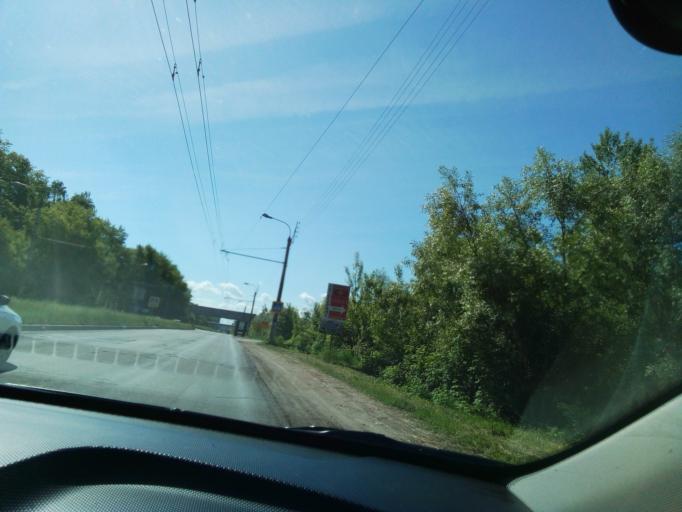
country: RU
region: Chuvashia
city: Novocheboksarsk
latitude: 56.0849
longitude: 47.5028
